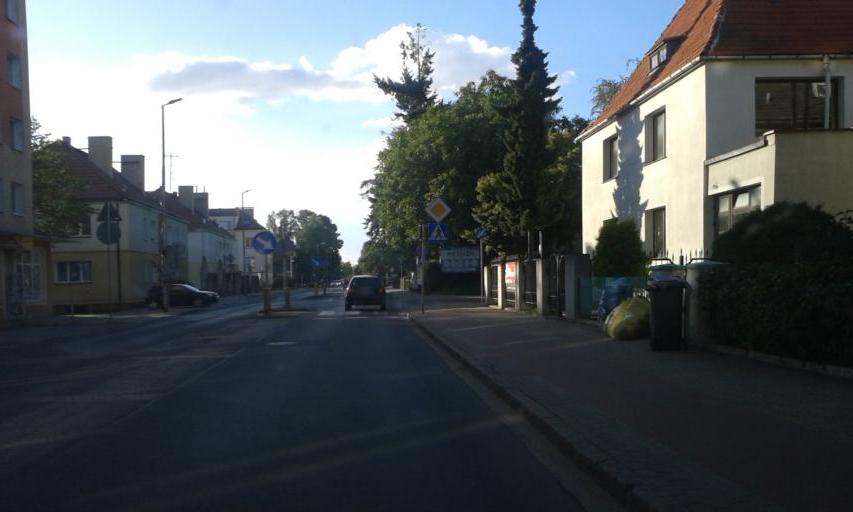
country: PL
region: West Pomeranian Voivodeship
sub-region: Koszalin
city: Koszalin
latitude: 54.1952
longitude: 16.2071
